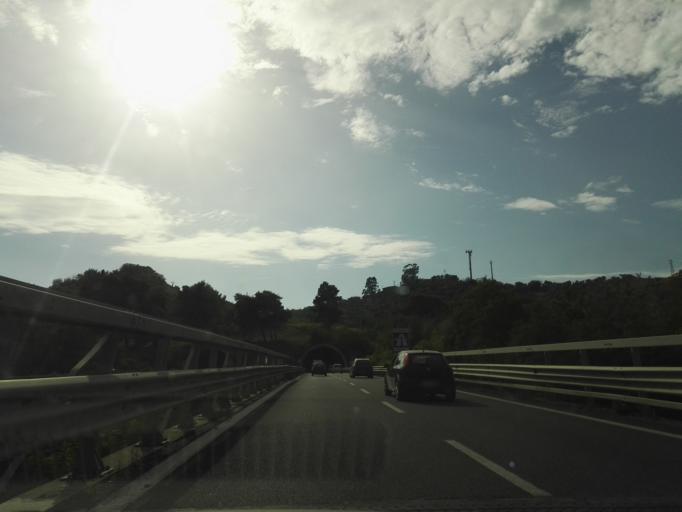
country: IT
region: Calabria
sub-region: Provincia di Catanzaro
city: Marcellinara
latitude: 38.9178
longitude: 16.4837
